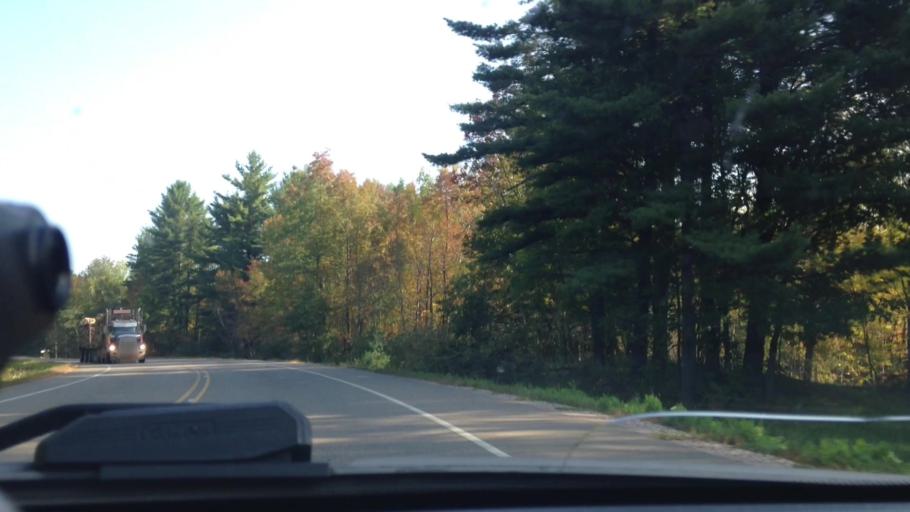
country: US
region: Michigan
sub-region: Dickinson County
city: Quinnesec
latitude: 45.8111
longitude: -87.9861
